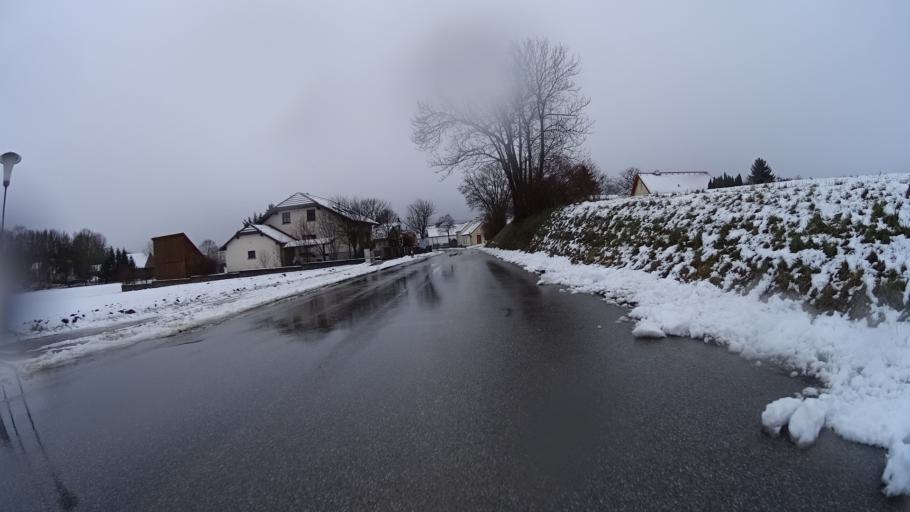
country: AT
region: Lower Austria
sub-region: Politischer Bezirk Korneuburg
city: Spillern
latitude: 48.3887
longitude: 16.2804
